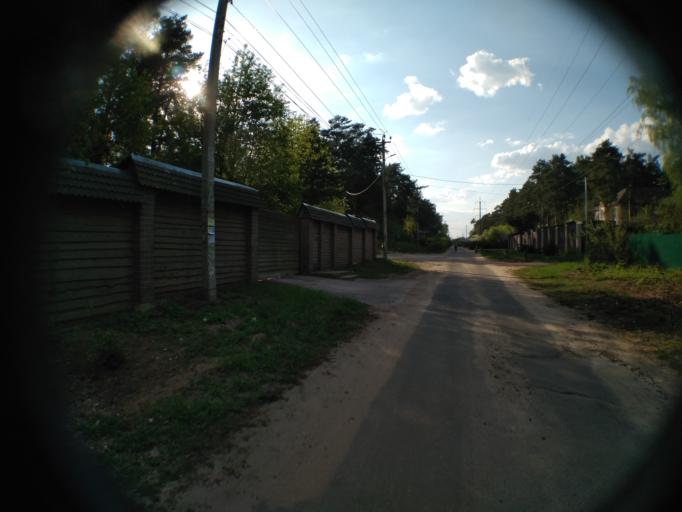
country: RU
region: Moskovskaya
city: Kratovo
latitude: 55.5797
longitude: 38.1663
